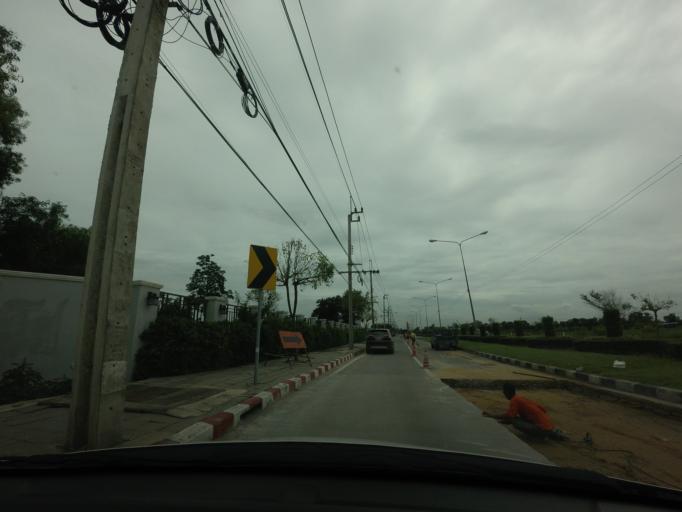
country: TH
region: Pathum Thani
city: Lam Luk Ka
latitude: 13.9149
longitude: 100.7806
